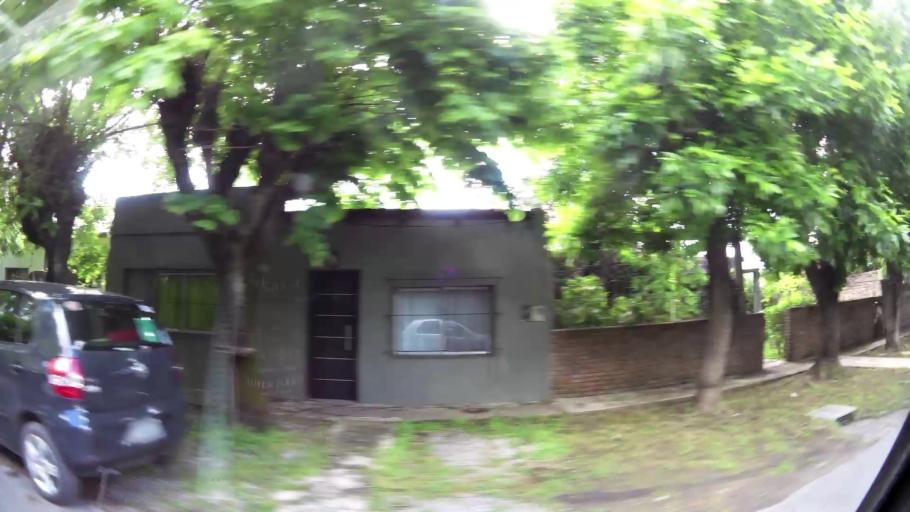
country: AR
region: Buenos Aires
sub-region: Partido de Quilmes
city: Quilmes
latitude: -34.8287
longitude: -58.1844
